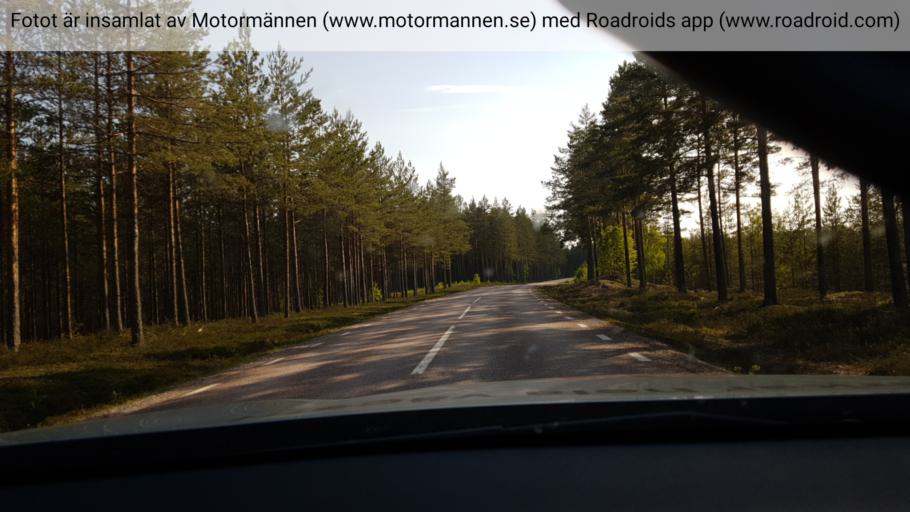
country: SE
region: Gaevleborg
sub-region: Sandvikens Kommun
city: Arsunda
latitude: 60.4701
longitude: 16.7085
